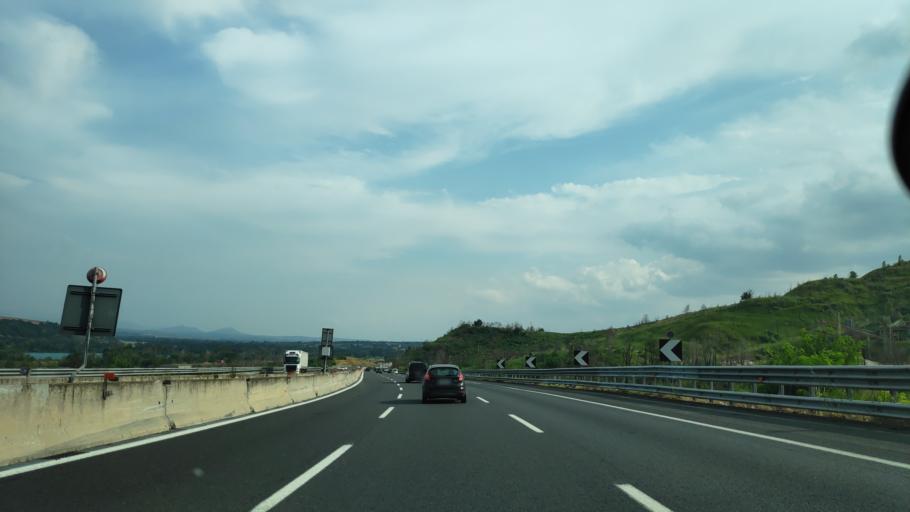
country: IT
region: Latium
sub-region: Citta metropolitana di Roma Capitale
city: Civitella San Paolo
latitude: 42.2011
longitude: 12.6025
